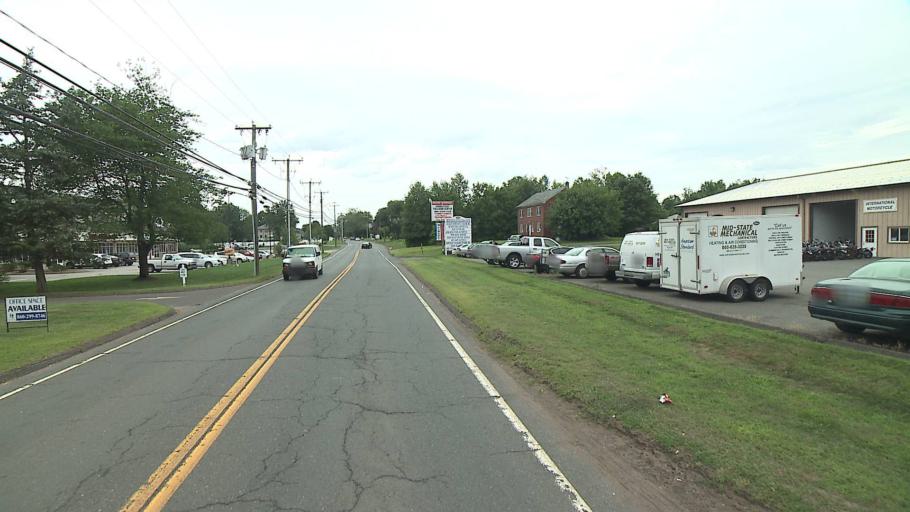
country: US
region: Connecticut
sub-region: Middlesex County
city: Middletown
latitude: 41.5798
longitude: -72.6726
